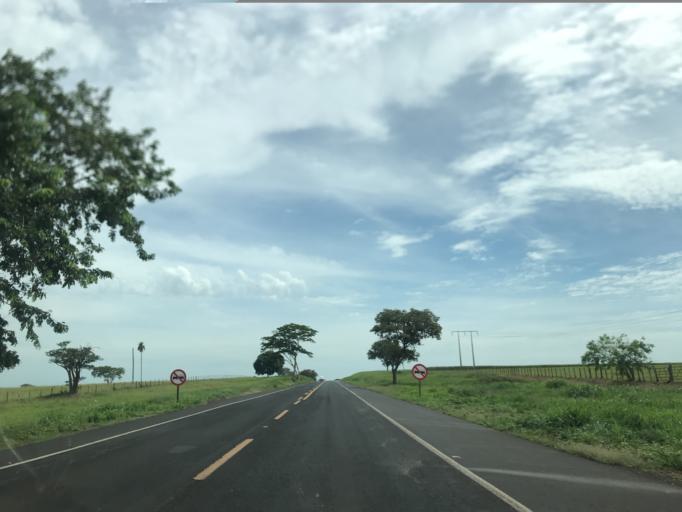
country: BR
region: Sao Paulo
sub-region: Nova Granada
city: Nova Granada
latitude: -20.3869
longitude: -49.2350
